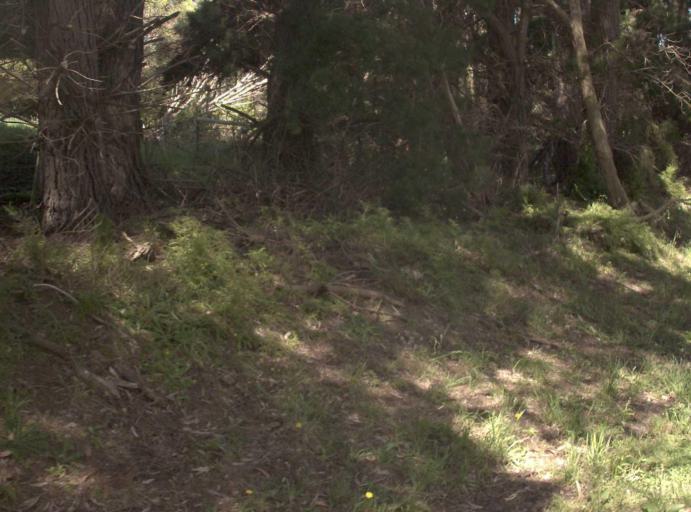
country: AU
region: Victoria
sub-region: Bass Coast
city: North Wonthaggi
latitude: -38.7762
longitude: 146.0748
